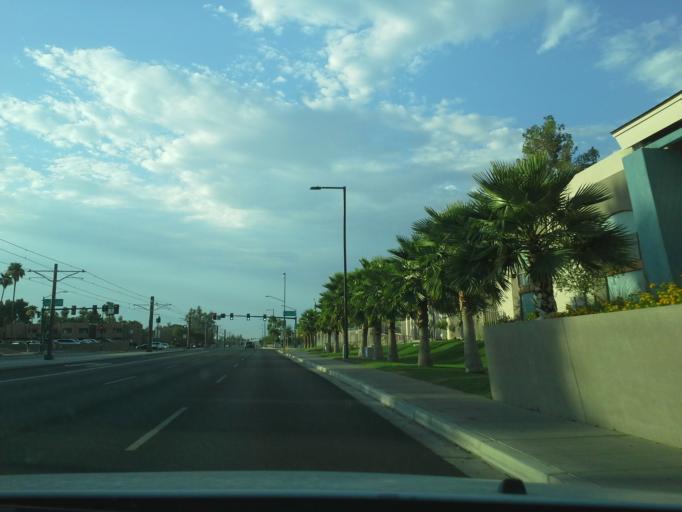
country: US
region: Arizona
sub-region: Maricopa County
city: Glendale
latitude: 33.5557
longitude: -112.0995
